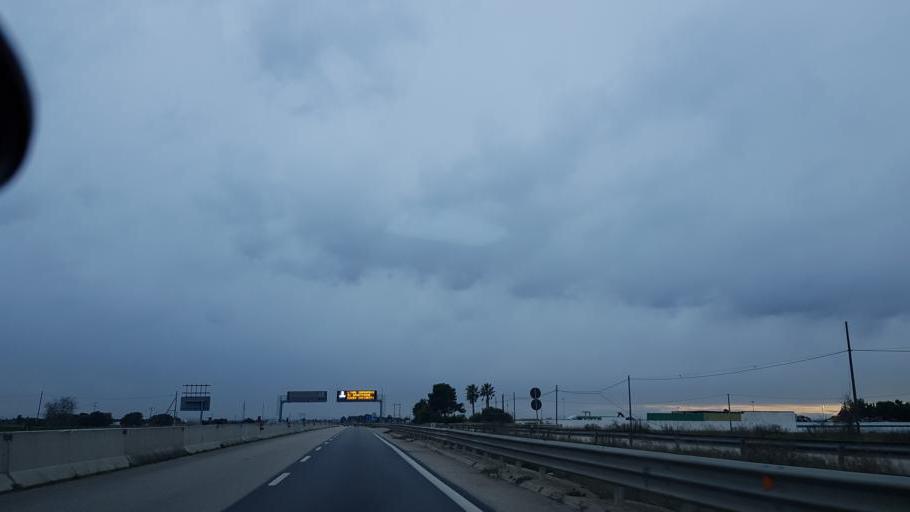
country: IT
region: Apulia
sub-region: Provincia di Brindisi
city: Brindisi
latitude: 40.6153
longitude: 17.9013
